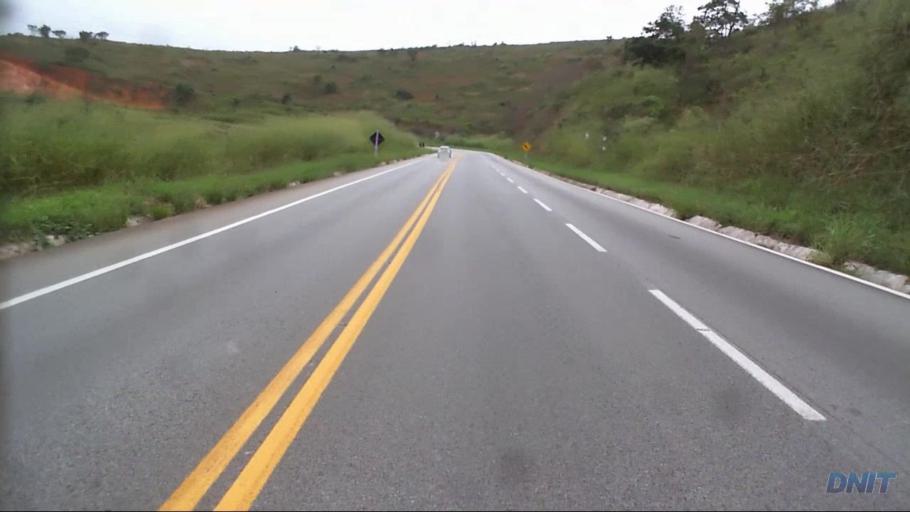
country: BR
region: Minas Gerais
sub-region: Nova Era
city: Nova Era
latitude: -19.7921
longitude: -43.0556
